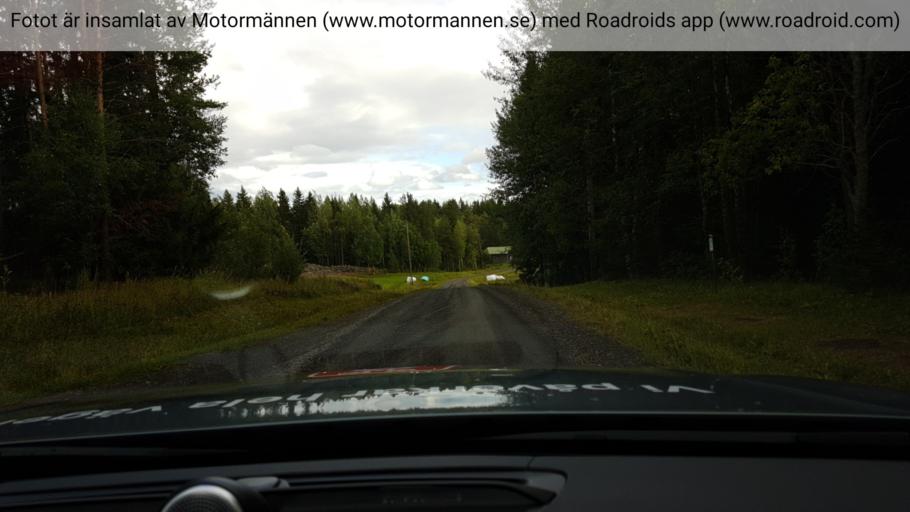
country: SE
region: Jaemtland
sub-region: OEstersunds Kommun
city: Lit
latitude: 63.7734
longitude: 14.6459
